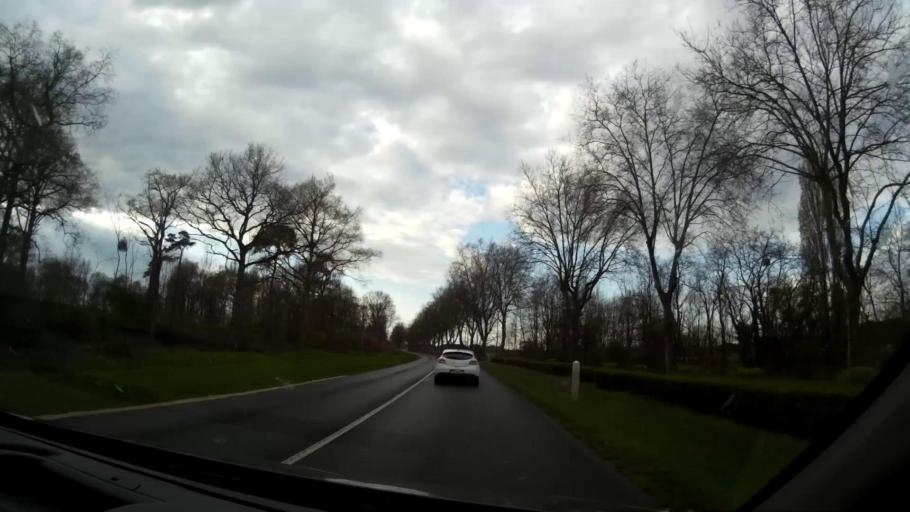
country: FR
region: Centre
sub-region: Departement du Loir-et-Cher
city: Cormeray
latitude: 47.4711
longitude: 1.4236
